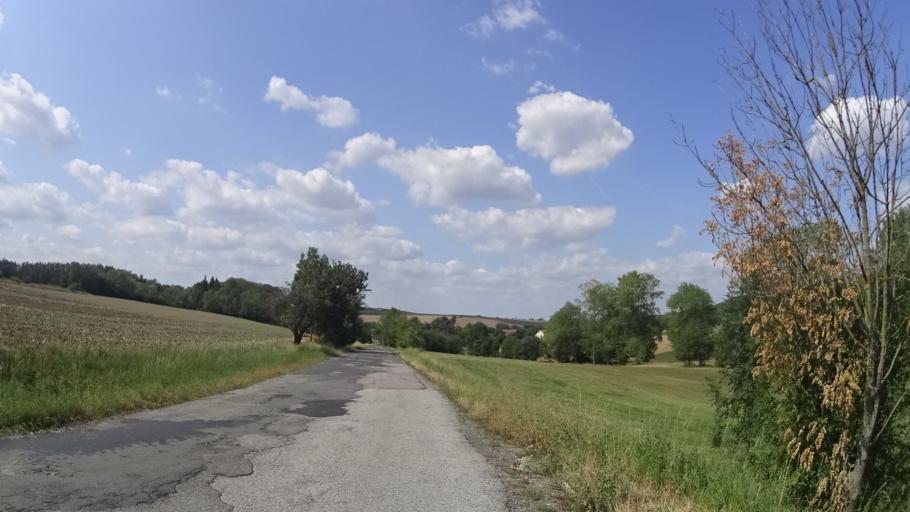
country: CZ
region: Kralovehradecky
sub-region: Okres Jicin
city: Jicin
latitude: 50.3779
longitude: 15.3257
